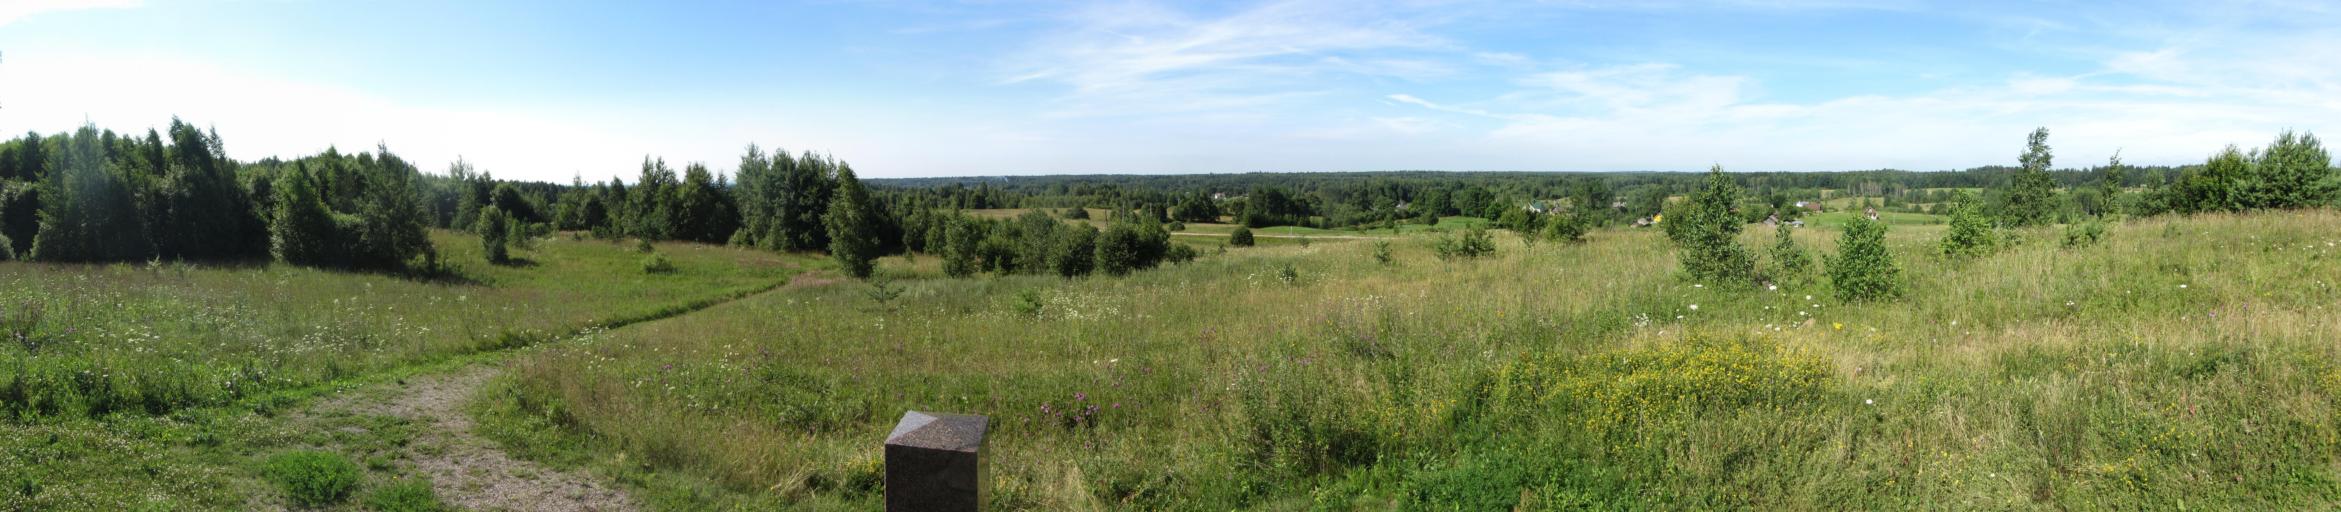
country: LT
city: Nemencine
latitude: 54.9292
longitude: 25.3160
